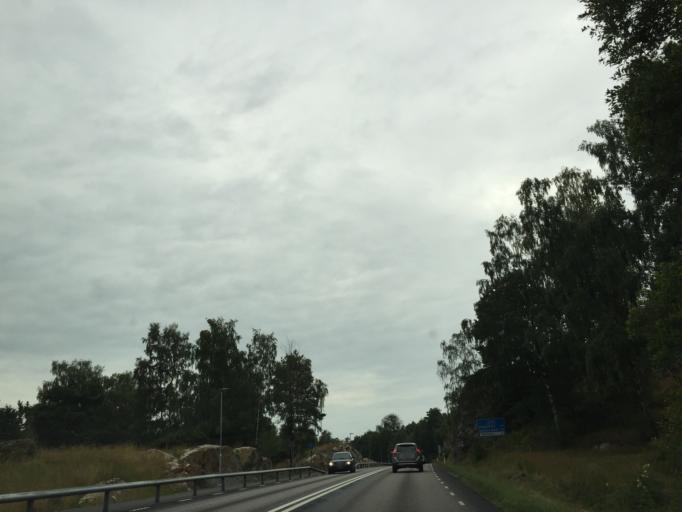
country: SE
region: Vaestra Goetaland
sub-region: Tjorns Kommun
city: Myggenas
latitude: 58.0554
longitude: 11.7587
